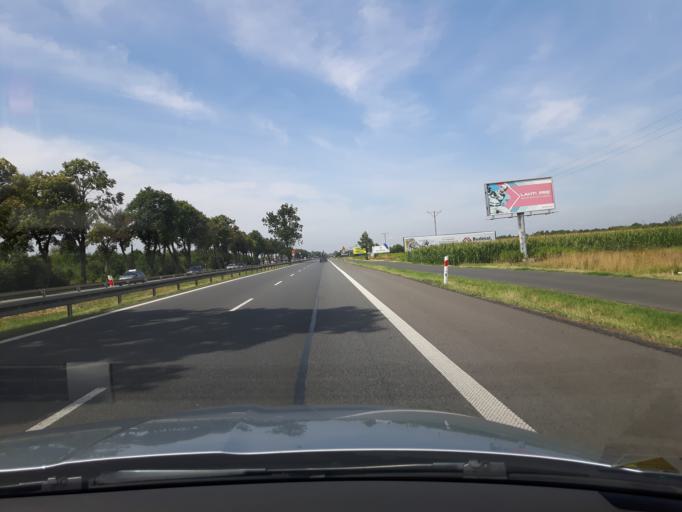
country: PL
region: Masovian Voivodeship
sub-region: Powiat nowodworski
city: Nowy Dwor Mazowiecki
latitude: 52.3821
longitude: 20.7595
